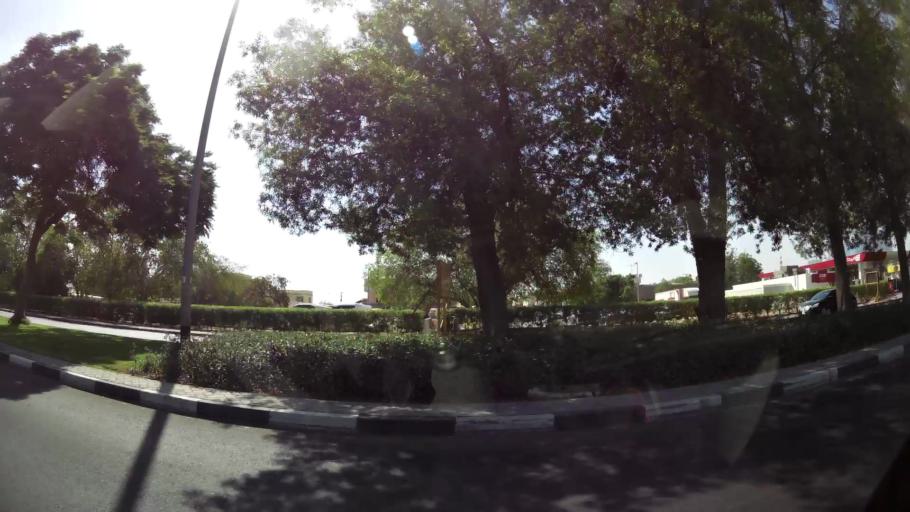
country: AE
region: Ash Shariqah
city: Sharjah
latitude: 25.2449
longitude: 55.2838
